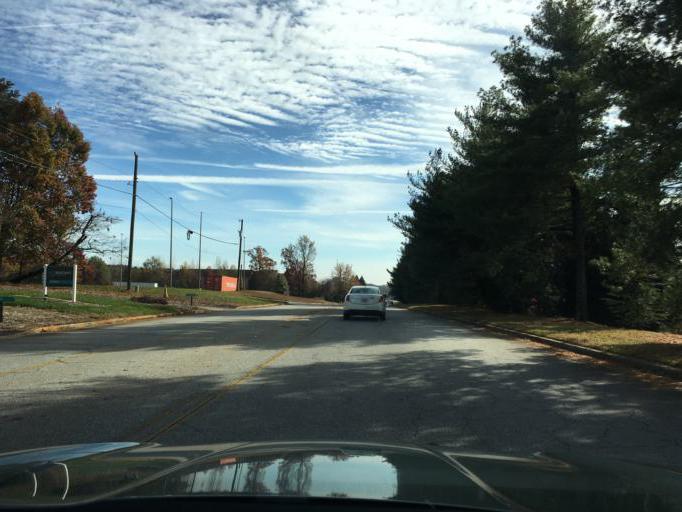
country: US
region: South Carolina
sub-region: Greenville County
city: Wade Hampton
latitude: 34.8465
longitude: -82.3322
